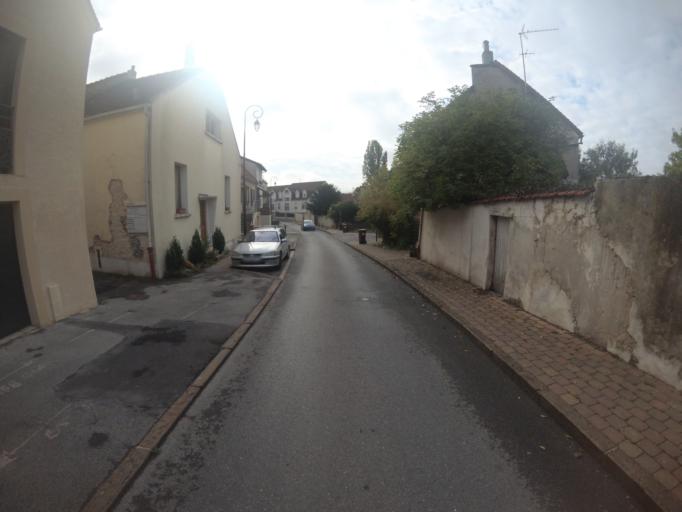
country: FR
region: Ile-de-France
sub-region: Departement de Seine-et-Marne
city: Montevrain
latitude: 48.8724
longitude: 2.7473
